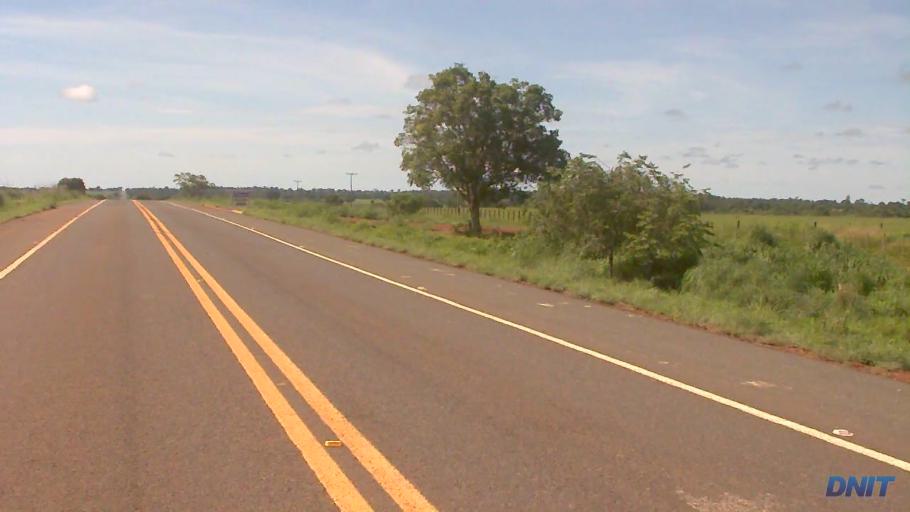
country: BR
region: Goias
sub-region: Sao Miguel Do Araguaia
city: Sao Miguel do Araguaia
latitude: -13.3680
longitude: -50.1445
